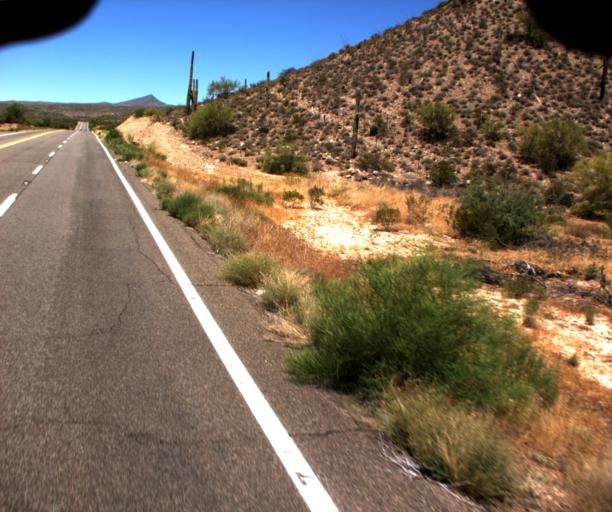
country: US
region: Arizona
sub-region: Pinal County
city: Kearny
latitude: 33.1341
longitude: -110.7845
